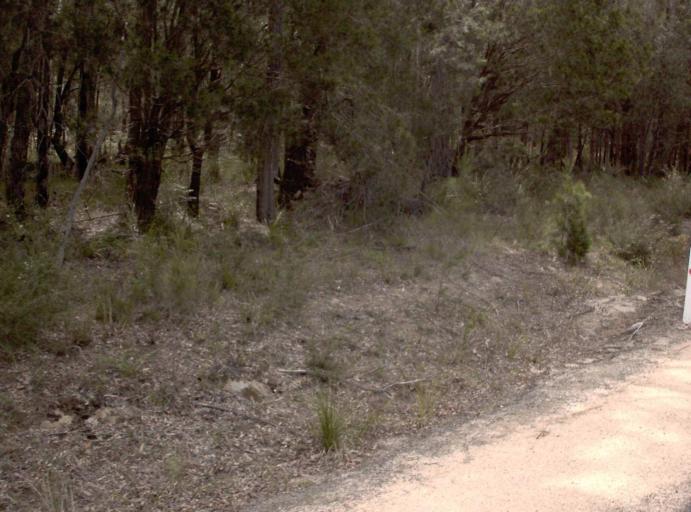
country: AU
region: New South Wales
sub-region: Bega Valley
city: Eden
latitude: -37.4296
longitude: 149.6448
